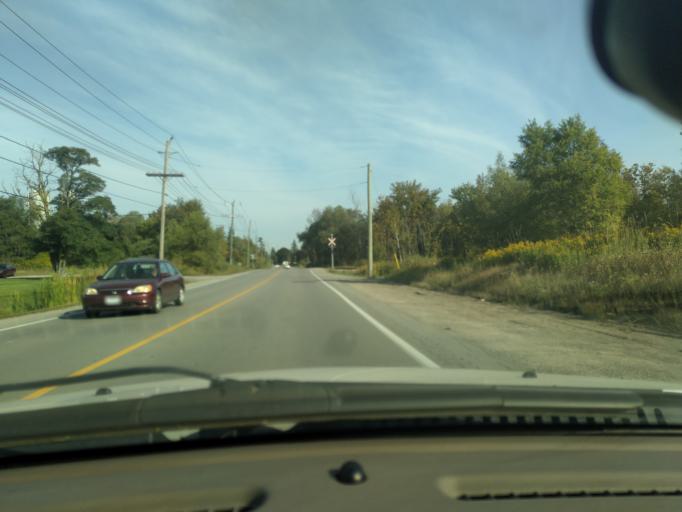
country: CA
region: Ontario
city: Barrie
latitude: 44.3557
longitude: -79.6657
